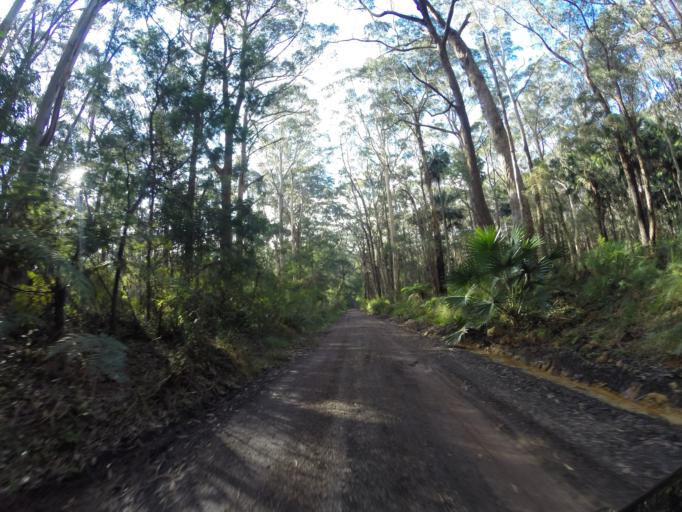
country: AU
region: New South Wales
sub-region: Wollongong
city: Cordeaux Heights
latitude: -34.4134
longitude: 150.7844
